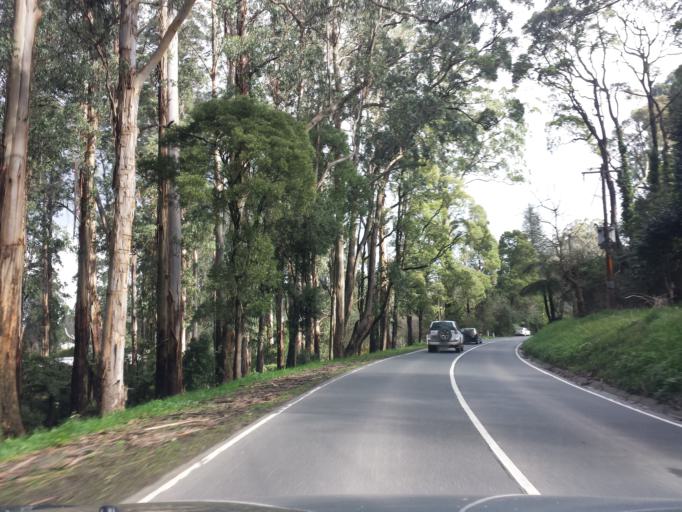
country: AU
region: Victoria
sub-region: Yarra Ranges
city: Ferny Creek
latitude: -37.8778
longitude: 145.3422
